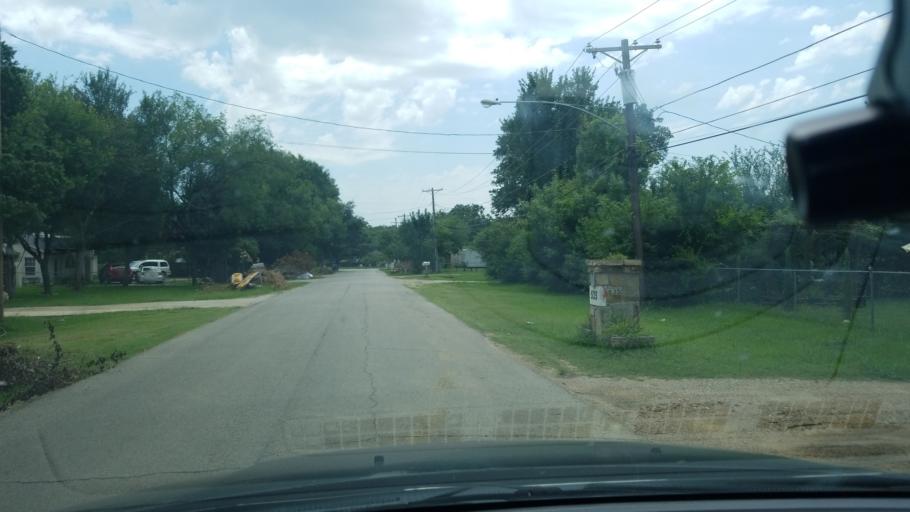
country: US
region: Texas
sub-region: Dallas County
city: Balch Springs
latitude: 32.7210
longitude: -96.6585
